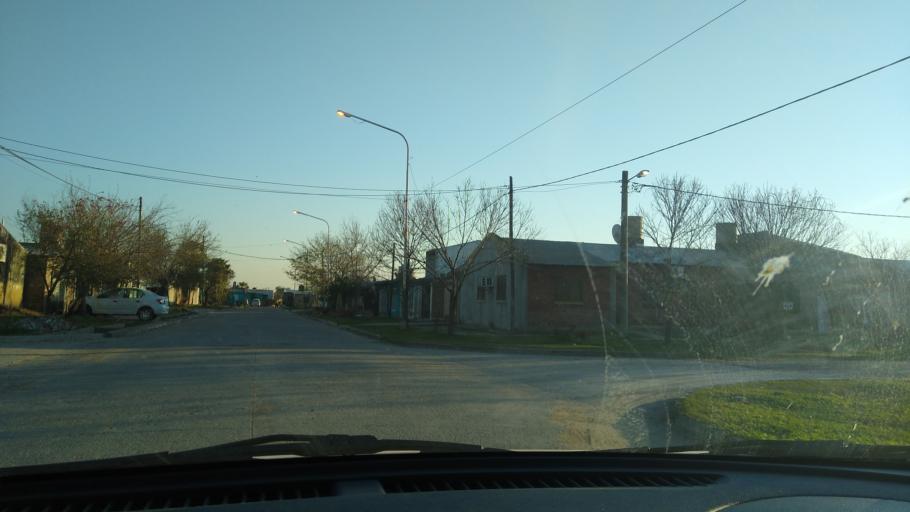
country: AR
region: Chaco
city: Puerto Vilelas
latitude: -27.5113
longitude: -58.9453
